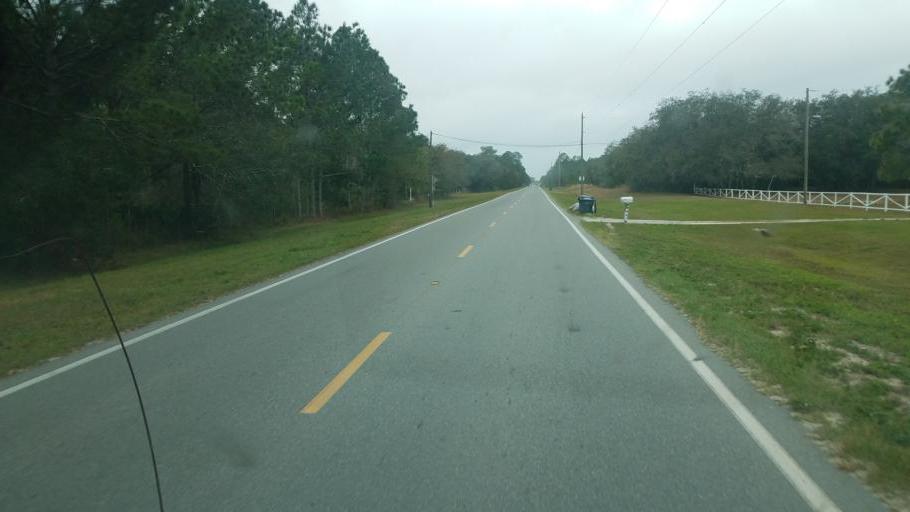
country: US
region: Florida
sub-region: Polk County
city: Polk City
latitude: 28.2586
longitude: -81.8109
